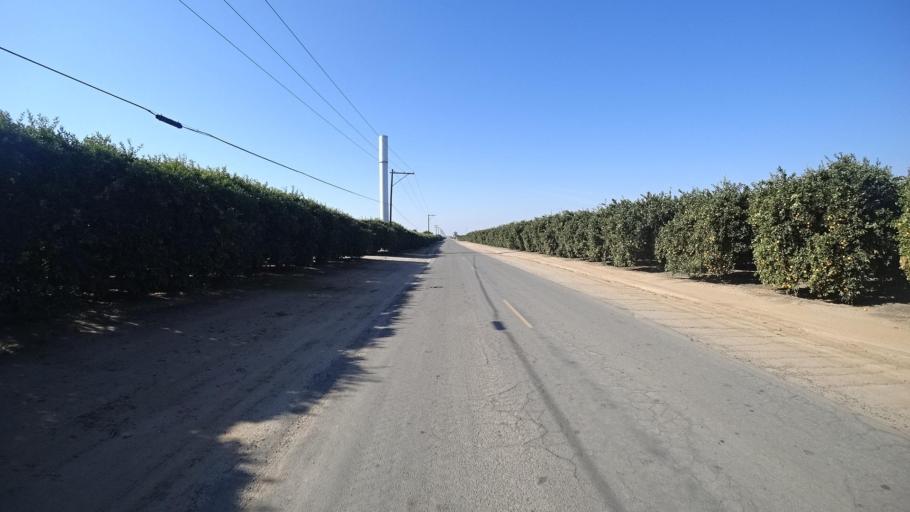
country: US
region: California
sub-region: Tulare County
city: Richgrove
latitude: 35.7183
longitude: -119.1358
